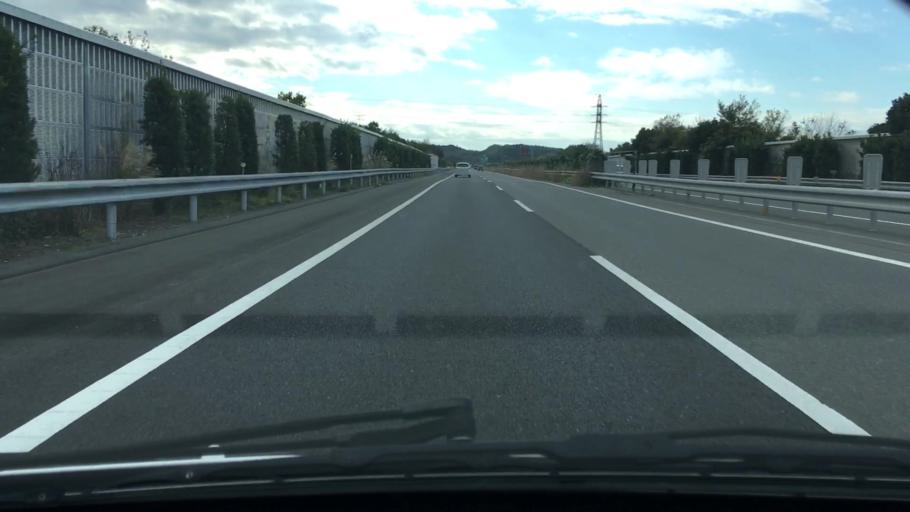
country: JP
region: Chiba
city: Kisarazu
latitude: 35.4006
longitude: 140.0066
